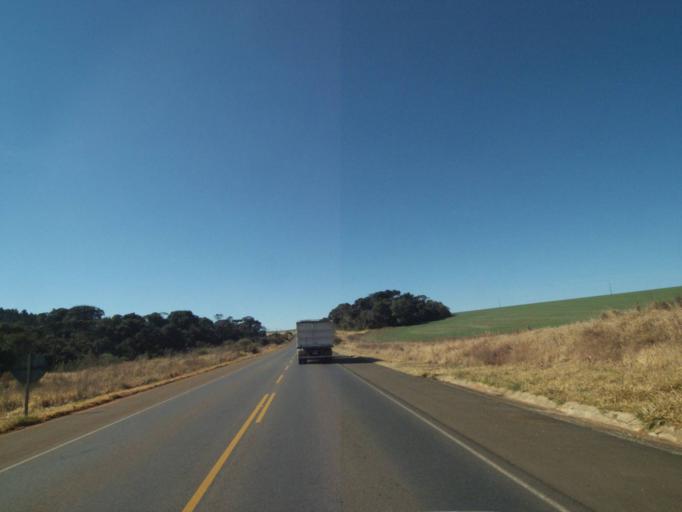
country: BR
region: Parana
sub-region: Tibagi
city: Tibagi
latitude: -24.4629
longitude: -50.4328
